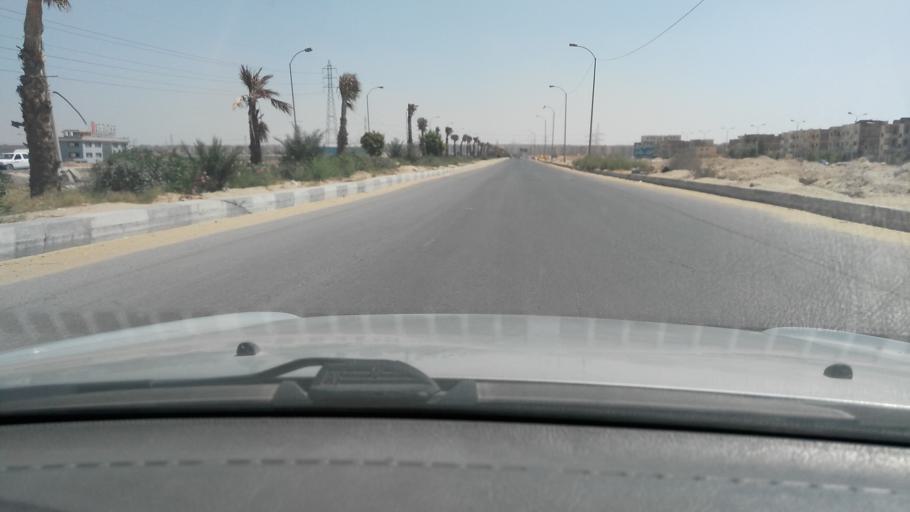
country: EG
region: Al Jizah
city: Madinat Sittah Uktubar
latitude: 29.9071
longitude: 30.9223
